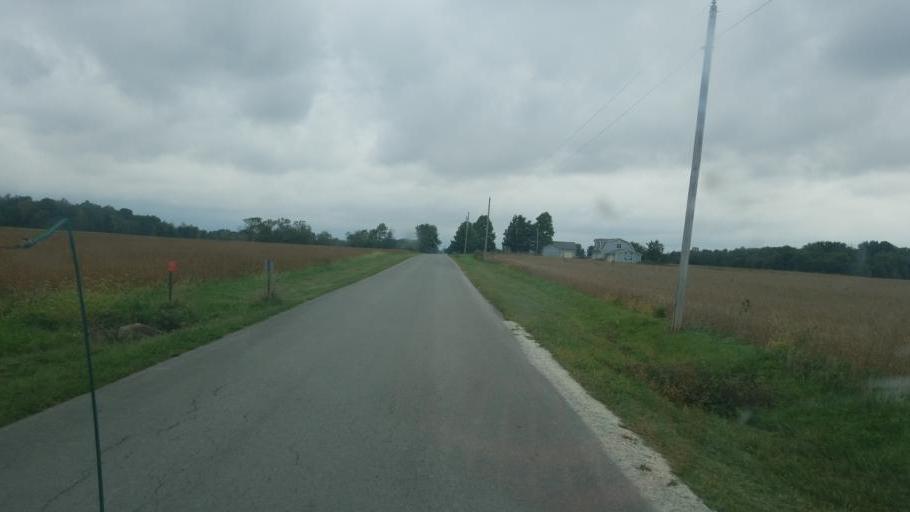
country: US
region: Ohio
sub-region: Seneca County
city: Fostoria
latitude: 41.0945
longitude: -83.5165
